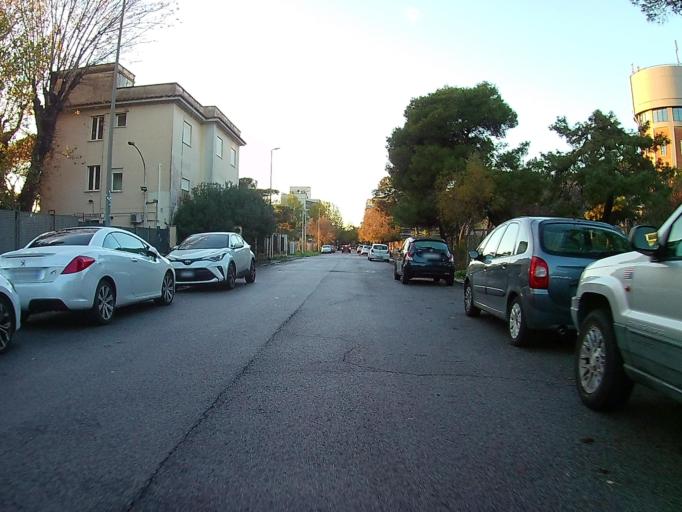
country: IT
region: Latium
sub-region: Citta metropolitana di Roma Capitale
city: Lido di Ostia
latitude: 41.7288
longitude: 12.2897
